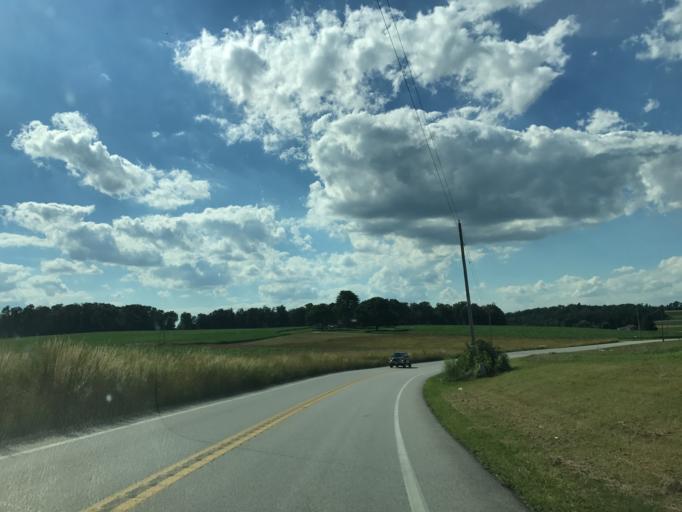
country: US
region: Pennsylvania
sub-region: York County
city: New Freedom
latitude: 39.7318
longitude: -76.7743
